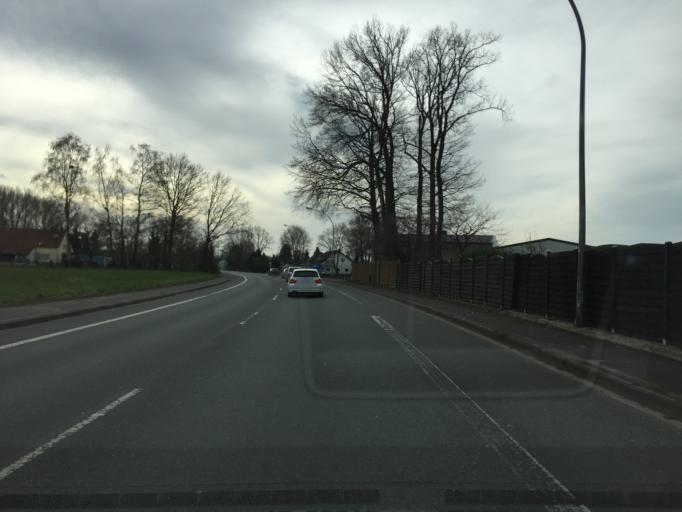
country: DE
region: North Rhine-Westphalia
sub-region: Regierungsbezirk Detmold
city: Lage
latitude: 52.0302
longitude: 8.7568
